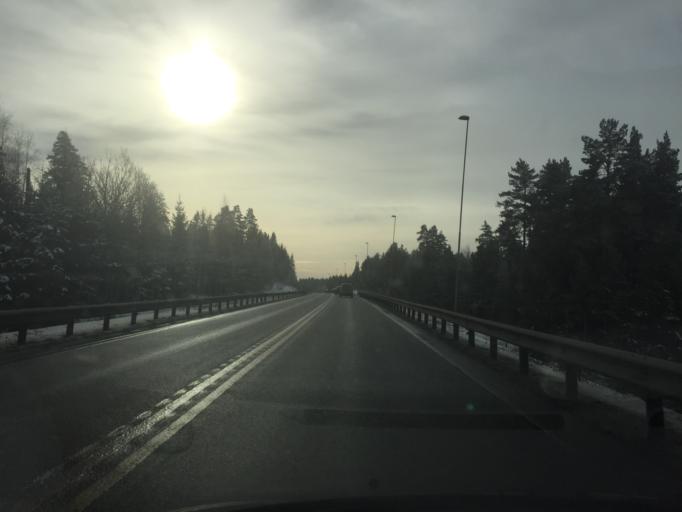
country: NO
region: Hedmark
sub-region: Loten
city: Loten
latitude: 60.7521
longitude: 11.3020
